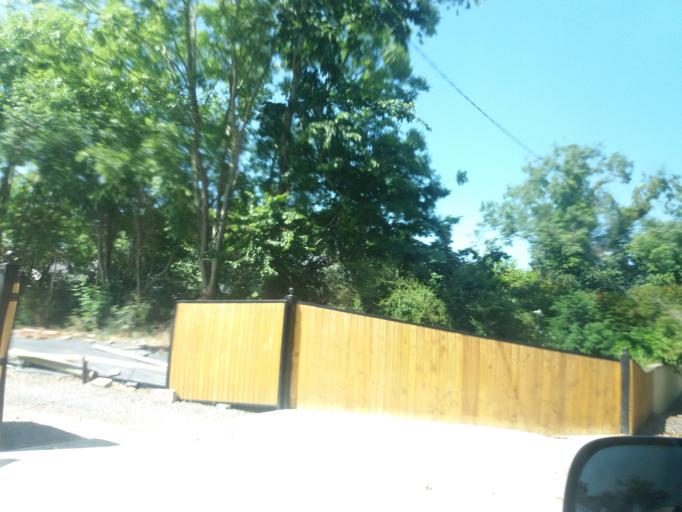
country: IE
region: Leinster
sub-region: An Mhi
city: Ashbourne
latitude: 53.5316
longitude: -6.3234
